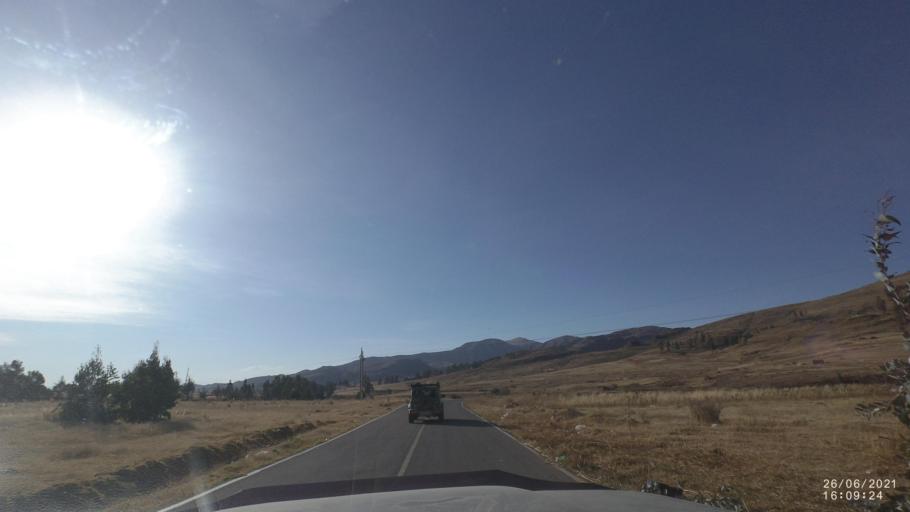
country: BO
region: Cochabamba
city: Arani
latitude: -17.8140
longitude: -65.7843
